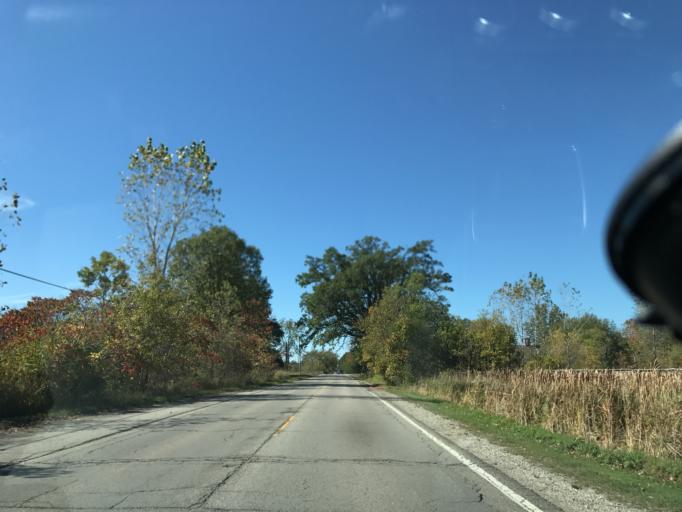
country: US
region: Michigan
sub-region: Oakland County
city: South Lyon
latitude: 42.4322
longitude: -83.6377
